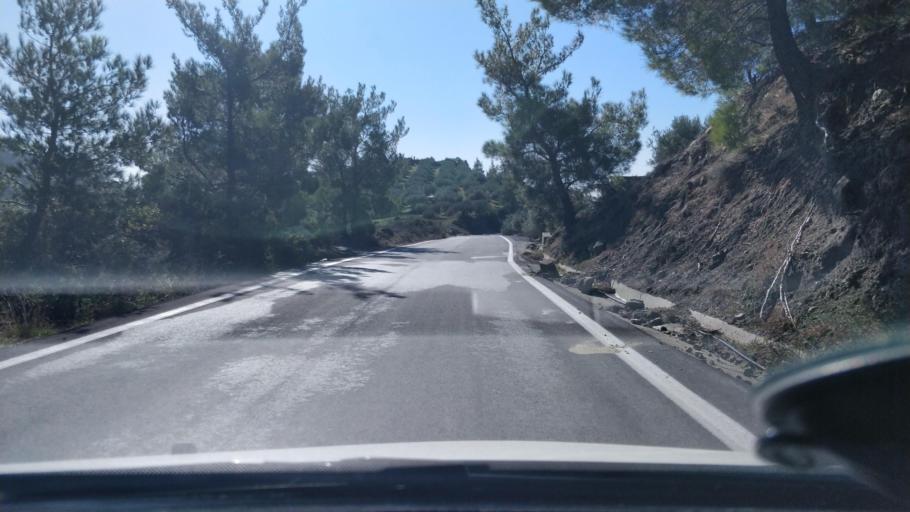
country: GR
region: Crete
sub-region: Nomos Irakleiou
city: Kastelli
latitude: 35.0286
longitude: 25.4495
